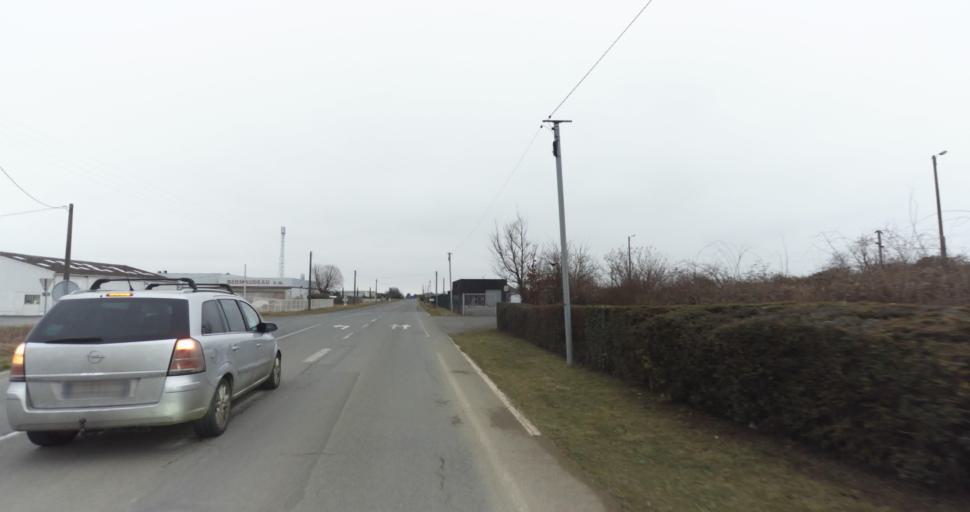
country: FR
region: Pays de la Loire
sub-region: Departement de Maine-et-Loire
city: Montreuil-Bellay
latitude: 47.1239
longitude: -0.1431
